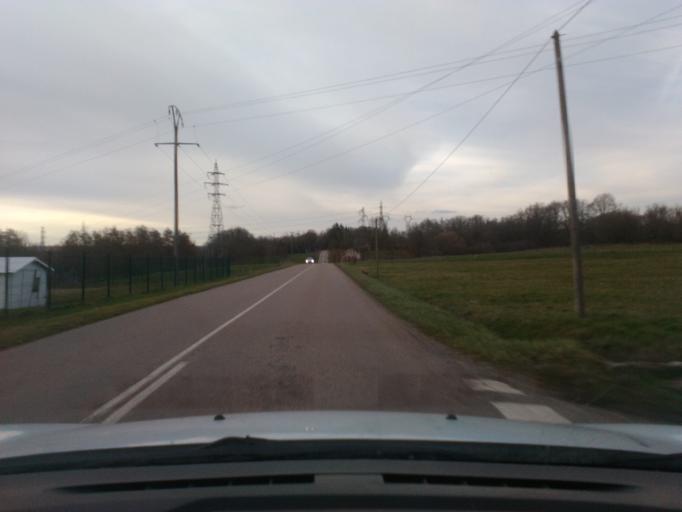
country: FR
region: Lorraine
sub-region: Departement des Vosges
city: Portieux
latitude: 48.3510
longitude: 6.3379
